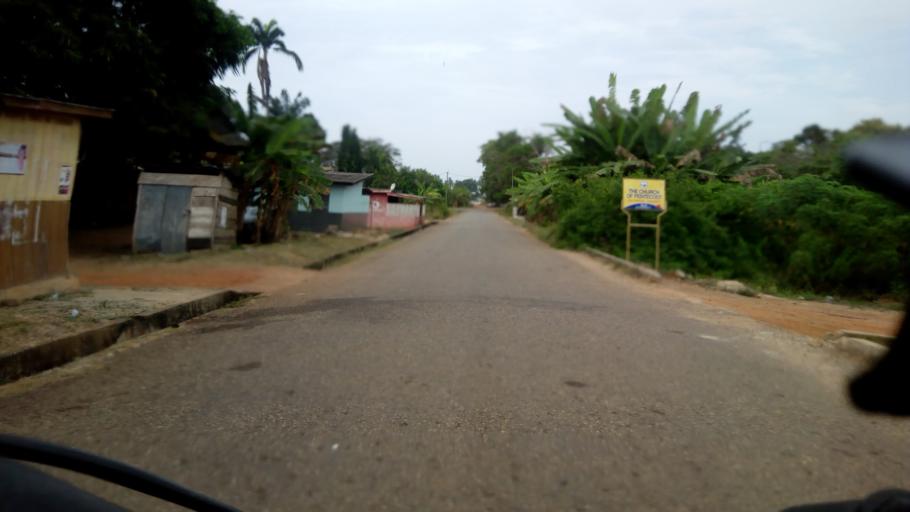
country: GH
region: Central
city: Cape Coast
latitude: 5.1050
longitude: -1.2790
